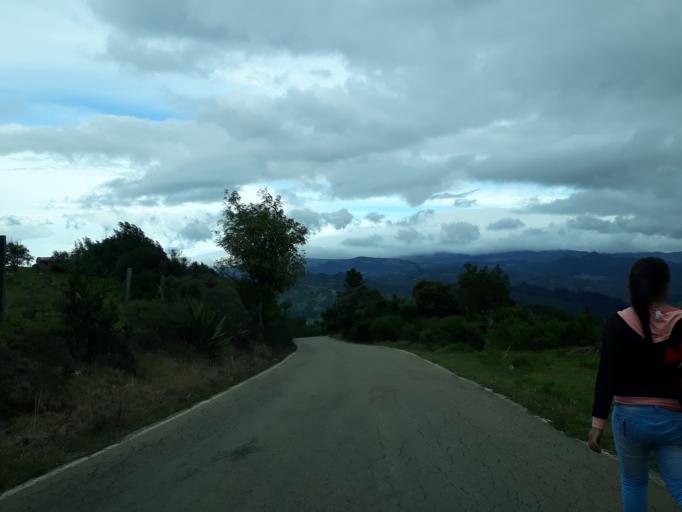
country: CO
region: Cundinamarca
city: Susa
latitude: 5.3960
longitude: -73.7854
